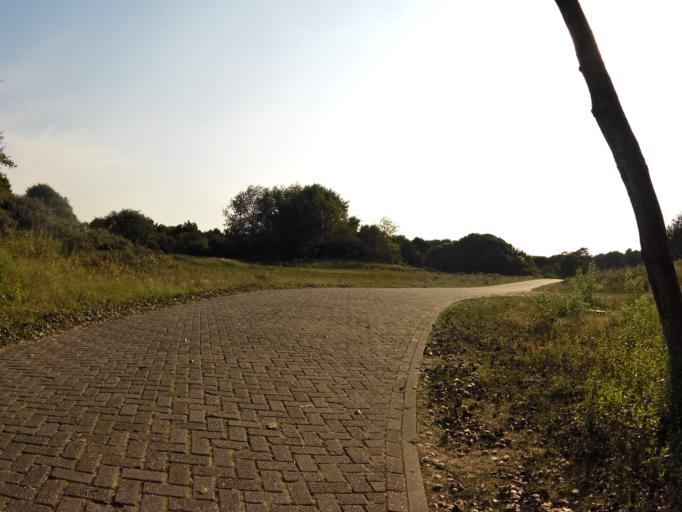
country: NL
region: North Holland
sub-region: Gemeente Castricum
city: Castricum
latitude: 52.5555
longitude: 4.6367
